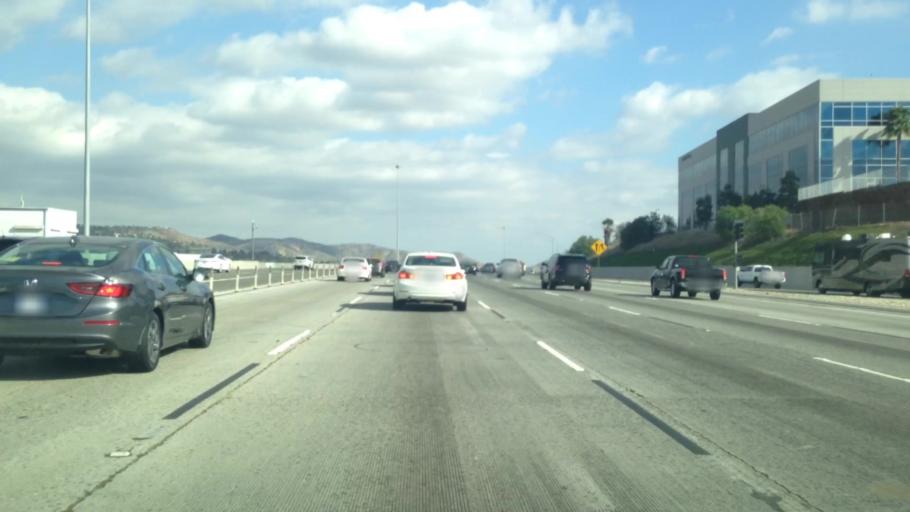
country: US
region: California
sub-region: Orange County
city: Yorba Linda
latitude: 33.8706
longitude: -117.7424
